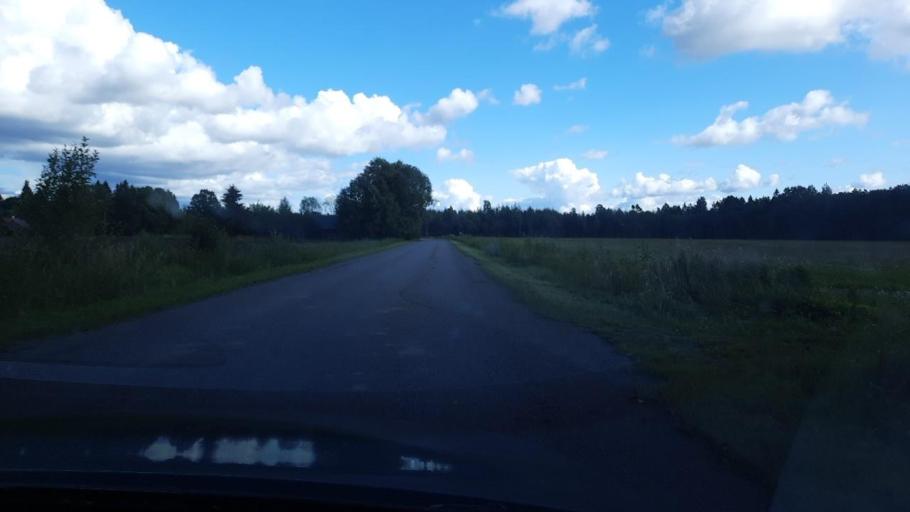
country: EE
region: Paernumaa
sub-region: Vaendra vald (alev)
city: Vandra
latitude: 58.4914
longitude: 24.9642
